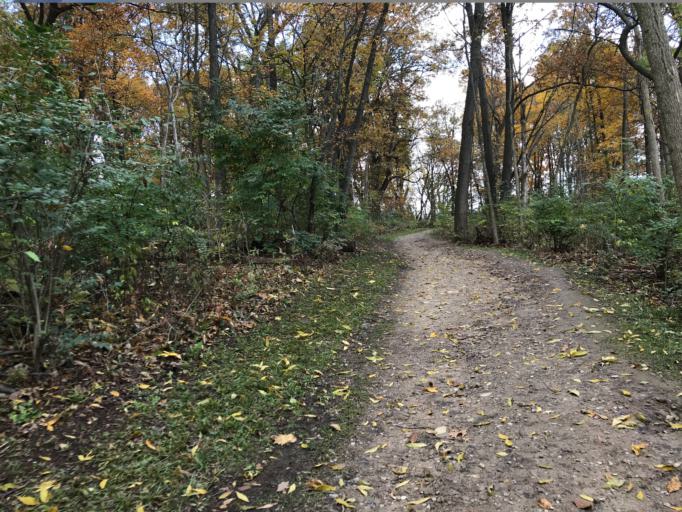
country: US
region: Michigan
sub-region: Washtenaw County
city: Ann Arbor
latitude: 42.2571
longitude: -83.7072
